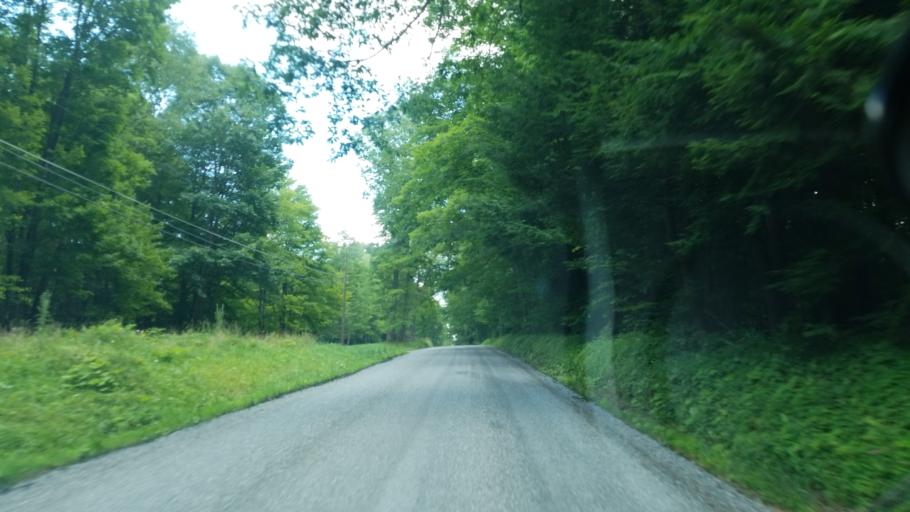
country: US
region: Pennsylvania
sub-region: Jefferson County
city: Brookville
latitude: 41.2298
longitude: -78.9917
